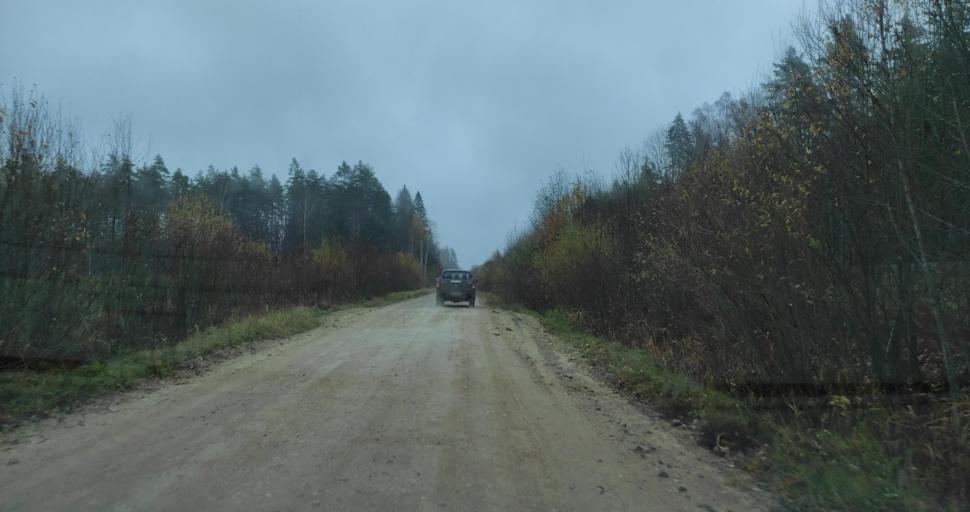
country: LV
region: Skrunda
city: Skrunda
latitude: 56.6939
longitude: 22.1034
